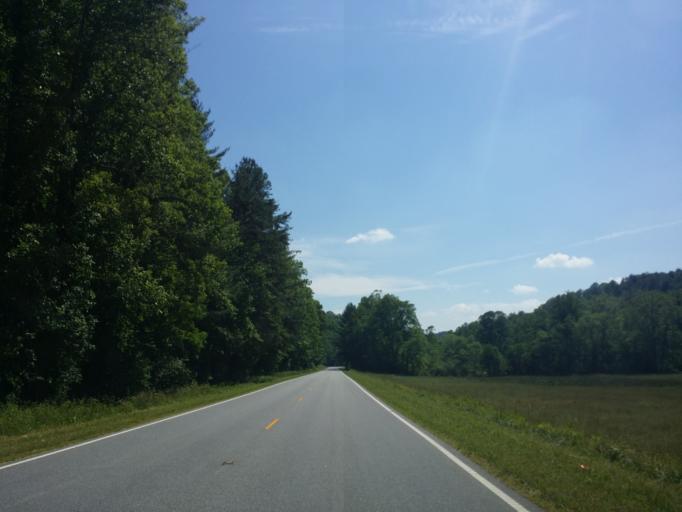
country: US
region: North Carolina
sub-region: Madison County
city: Marshall
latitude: 35.7053
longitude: -82.7875
